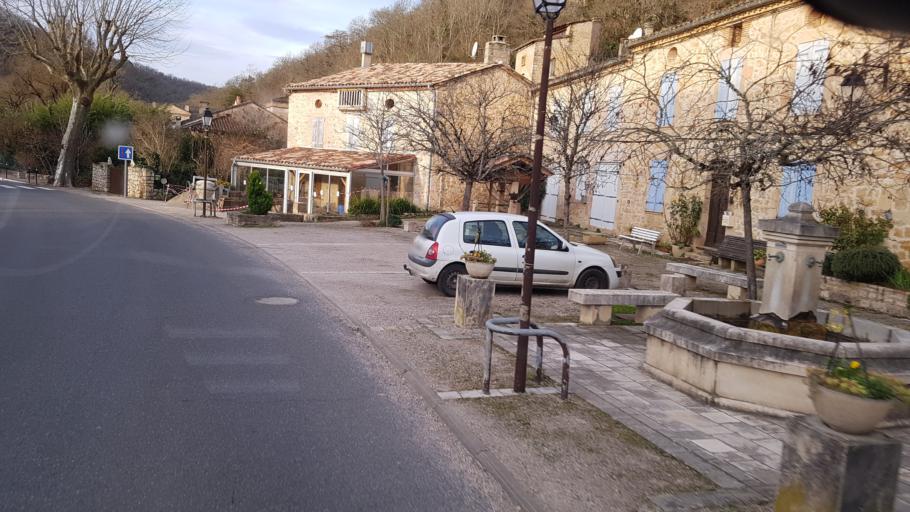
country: FR
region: Midi-Pyrenees
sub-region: Departement du Tarn-et-Garonne
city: Montricoux
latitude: 44.0031
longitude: 1.6897
